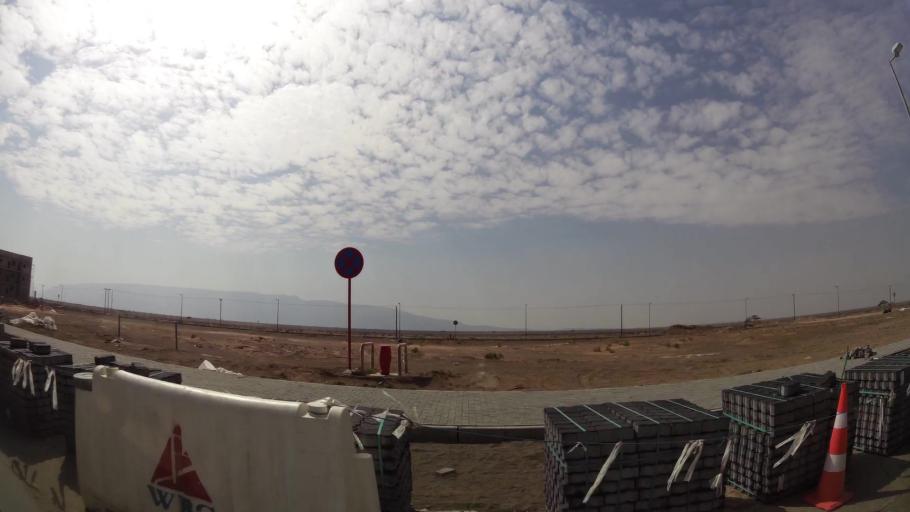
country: AE
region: Abu Dhabi
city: Al Ain
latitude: 24.1014
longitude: 55.8884
